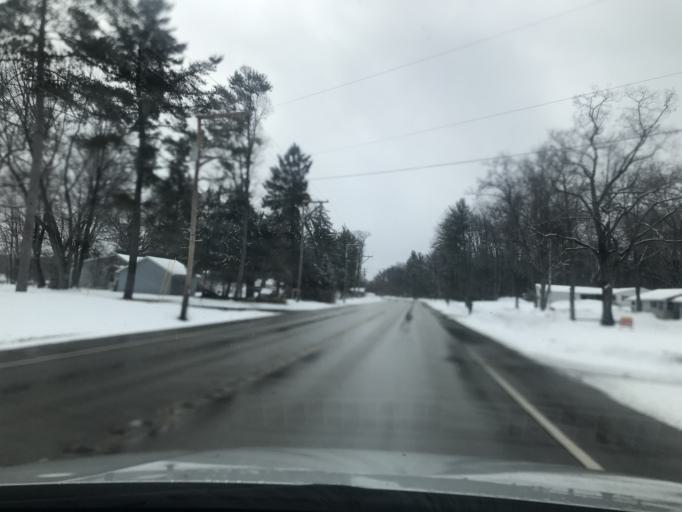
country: US
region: Wisconsin
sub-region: Marinette County
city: Peshtigo
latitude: 45.1714
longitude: -87.7372
